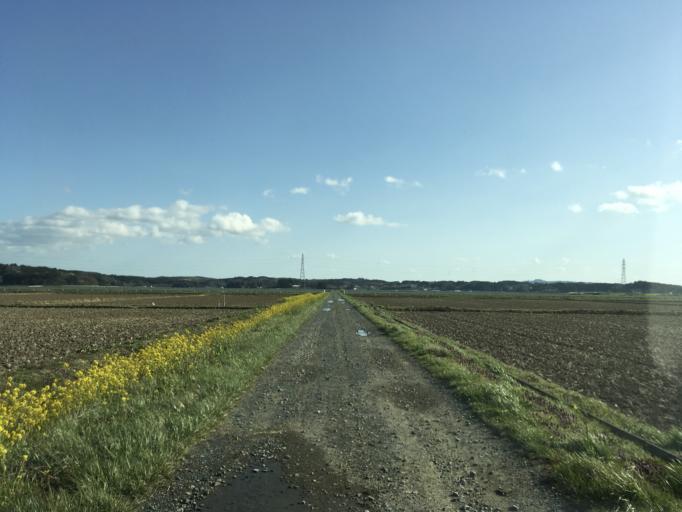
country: JP
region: Miyagi
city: Wakuya
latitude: 38.6602
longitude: 141.2414
